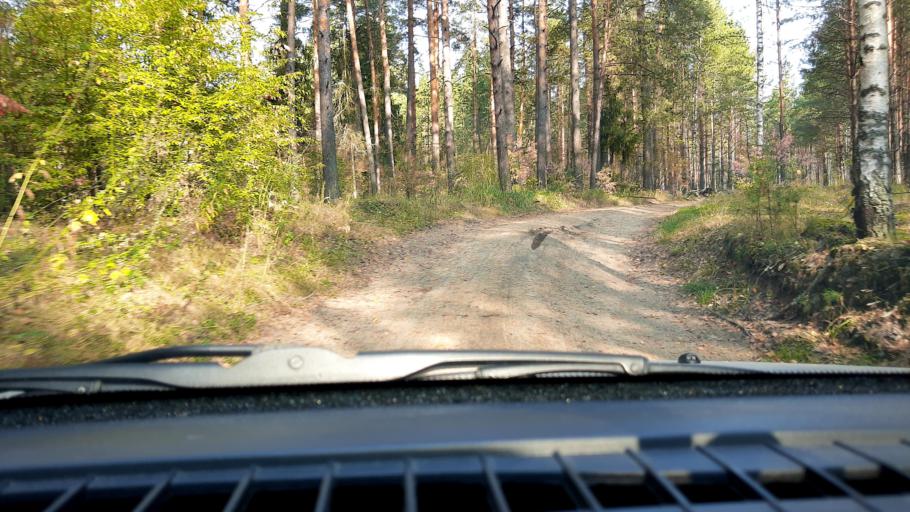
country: RU
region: Nizjnij Novgorod
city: Lukino
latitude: 56.3901
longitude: 43.6279
